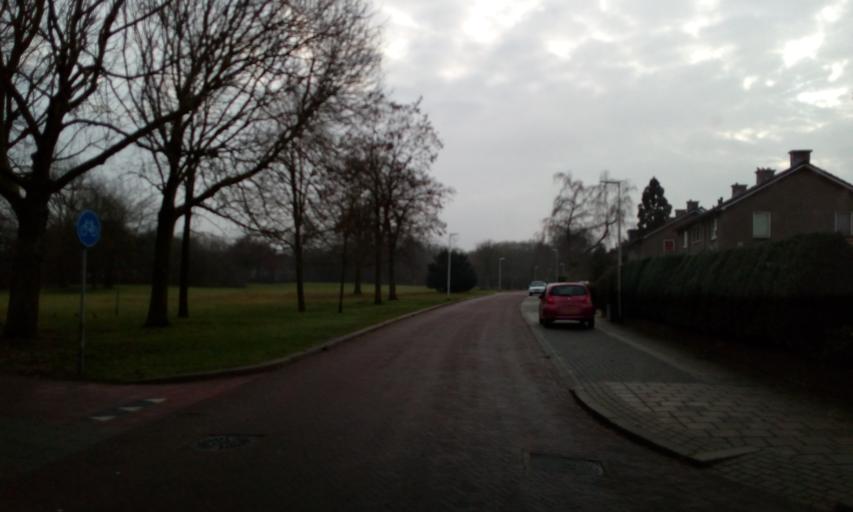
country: NL
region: North Holland
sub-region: Gemeente Bussum
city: Bussum
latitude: 52.2684
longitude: 5.1790
